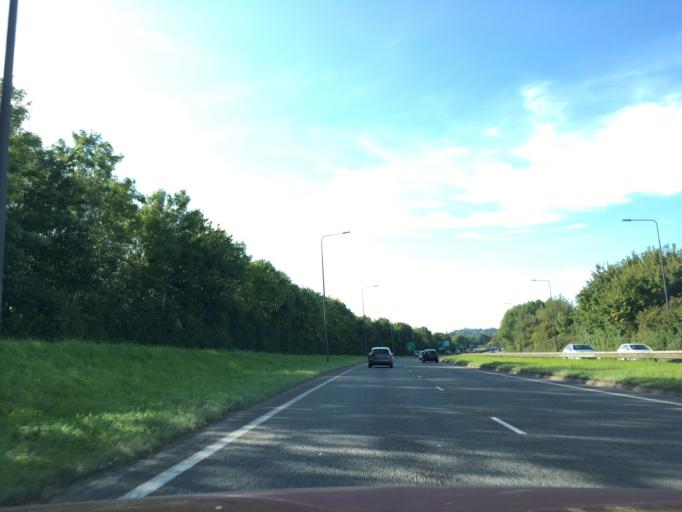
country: GB
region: England
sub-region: South Gloucestershire
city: Mangotsfield
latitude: 51.4956
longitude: -2.4756
